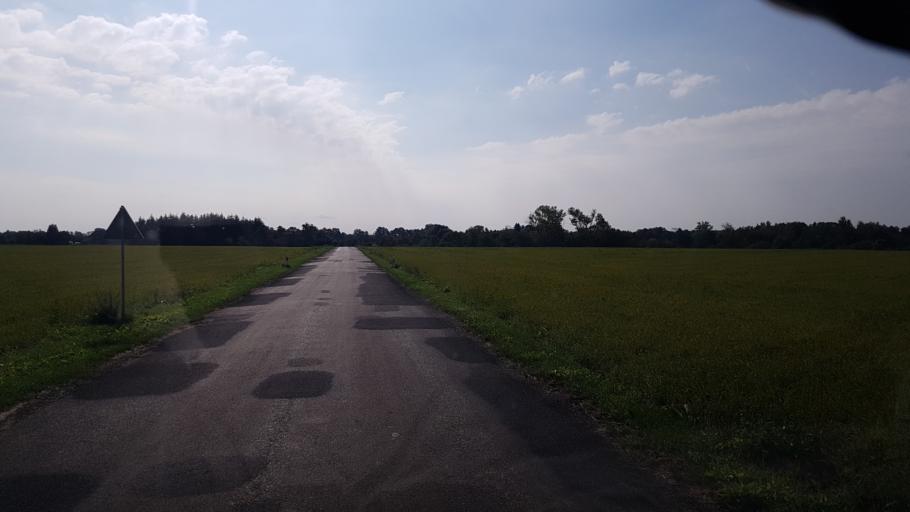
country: DE
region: Brandenburg
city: Luebben
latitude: 51.8718
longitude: 13.8527
